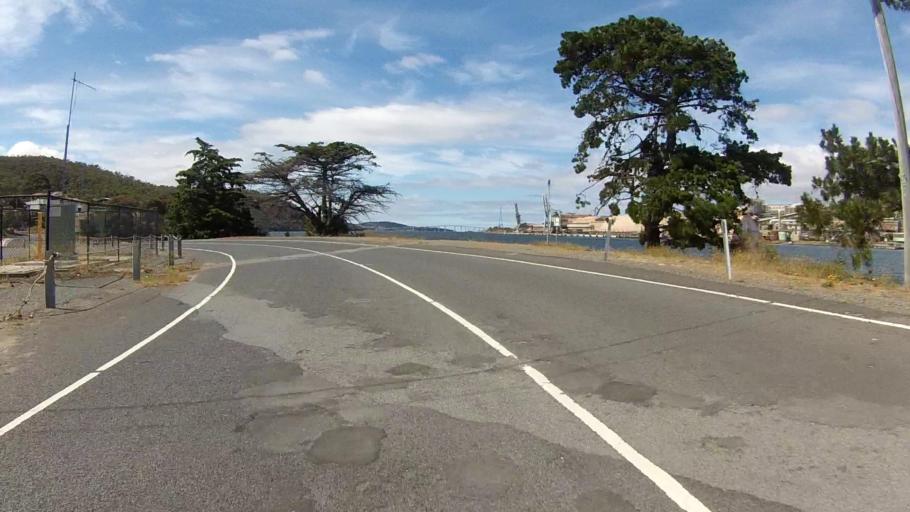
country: AU
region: Tasmania
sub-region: Glenorchy
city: Lutana
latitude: -42.8247
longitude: 147.3175
